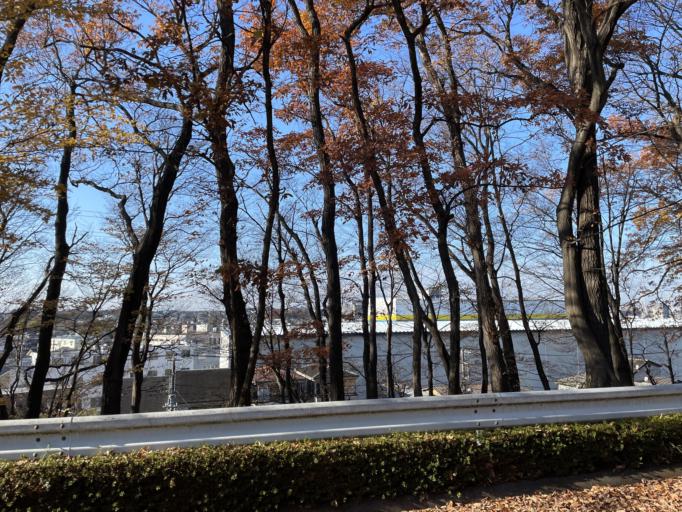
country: JP
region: Saitama
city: Asaka
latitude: 35.7829
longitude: 139.5801
